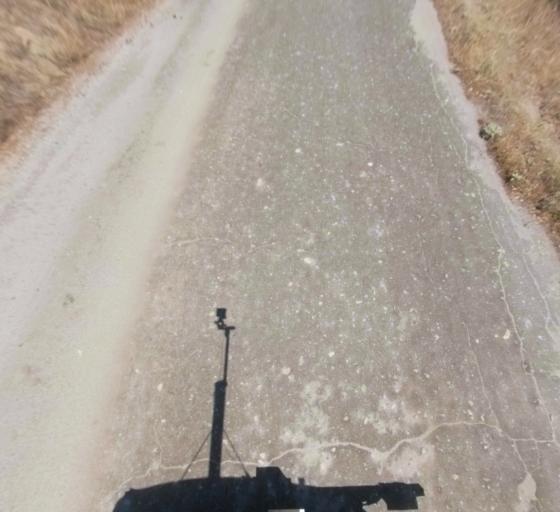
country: US
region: California
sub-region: Fresno County
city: Auberry
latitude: 37.1462
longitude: -119.4585
